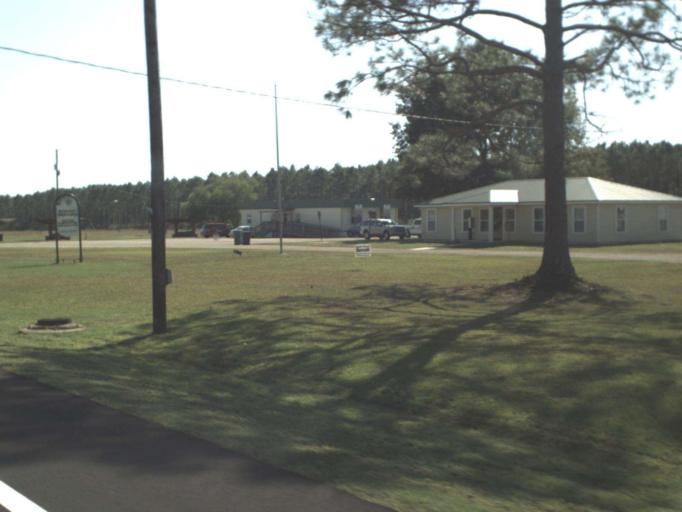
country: US
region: Alabama
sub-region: Covington County
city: Florala
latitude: 30.9690
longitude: -86.3017
